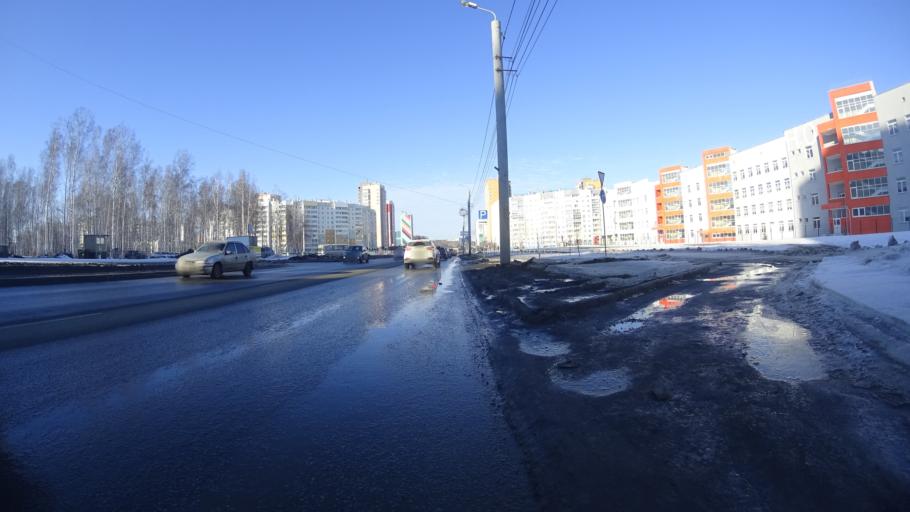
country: RU
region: Chelyabinsk
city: Roshchino
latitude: 55.2051
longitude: 61.2844
